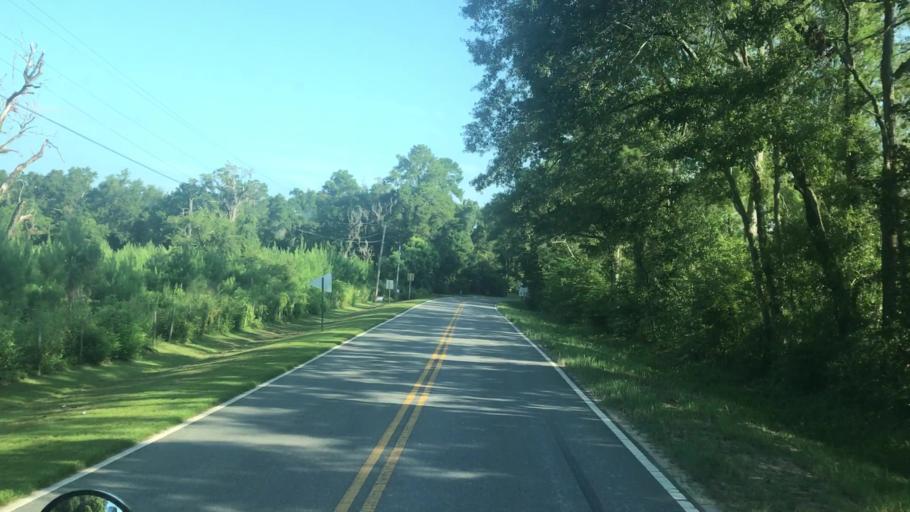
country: US
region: Florida
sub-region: Gadsden County
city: Quincy
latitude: 30.6069
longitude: -84.5729
